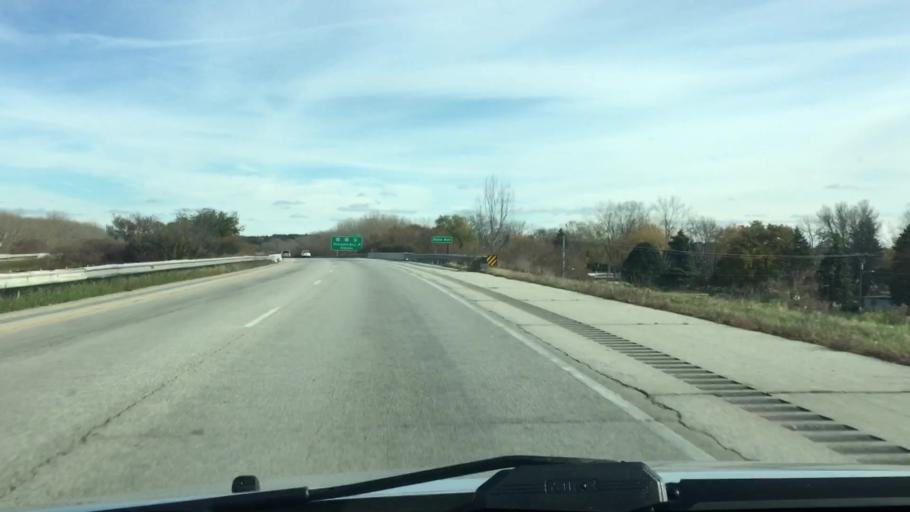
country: US
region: Wisconsin
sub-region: Brown County
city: Green Bay
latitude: 44.5200
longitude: -87.9689
